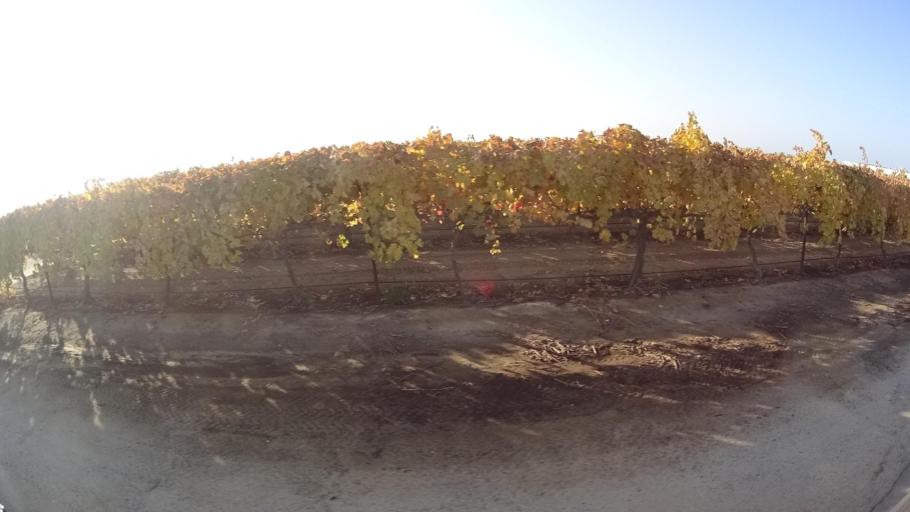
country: US
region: California
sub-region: Tulare County
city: Richgrove
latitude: 35.7762
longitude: -119.1210
